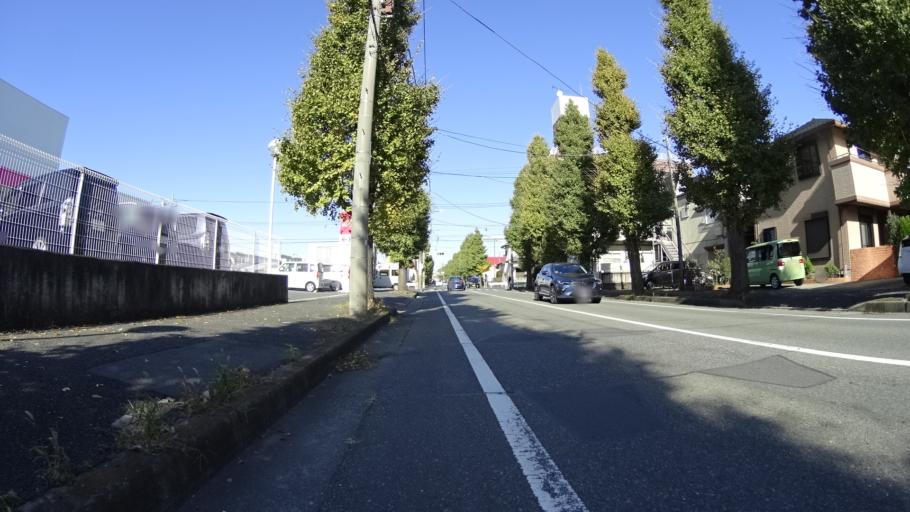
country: JP
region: Kanagawa
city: Zama
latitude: 35.5721
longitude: 139.3591
